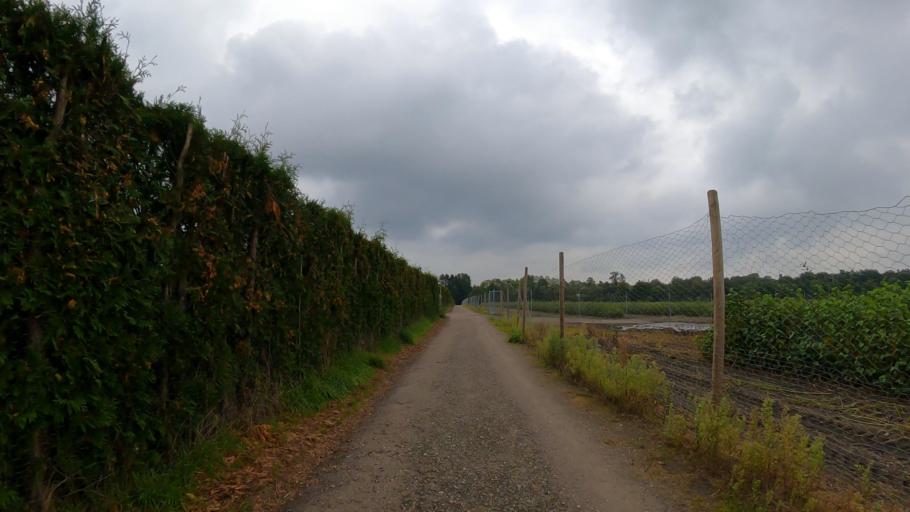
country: DE
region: Schleswig-Holstein
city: Halstenbek
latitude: 53.6320
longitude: 9.8304
